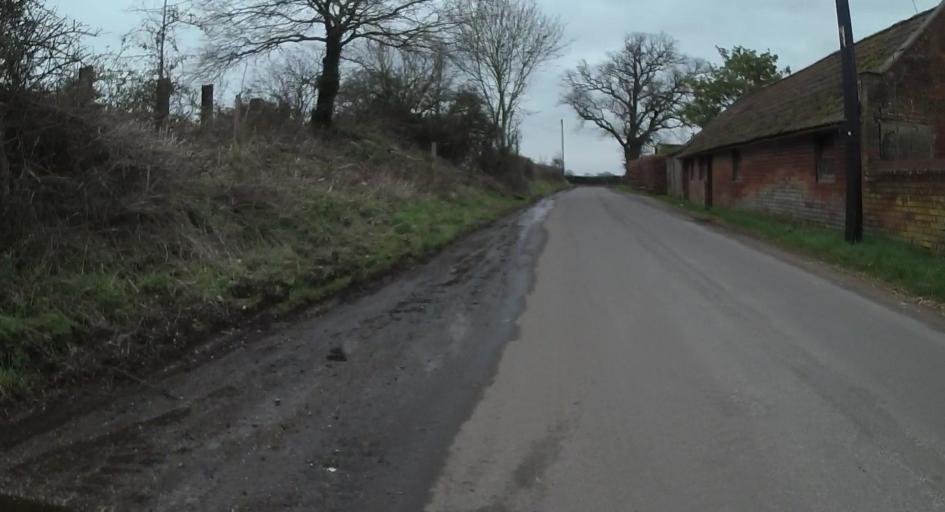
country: GB
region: England
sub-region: West Berkshire
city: Stratfield Mortimer
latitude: 51.3611
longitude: -1.0631
